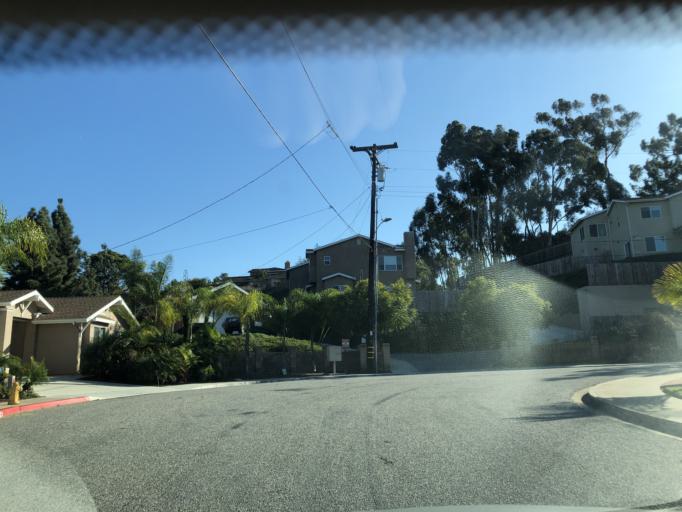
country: US
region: California
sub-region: San Diego County
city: Chula Vista
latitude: 32.6460
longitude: -117.0657
